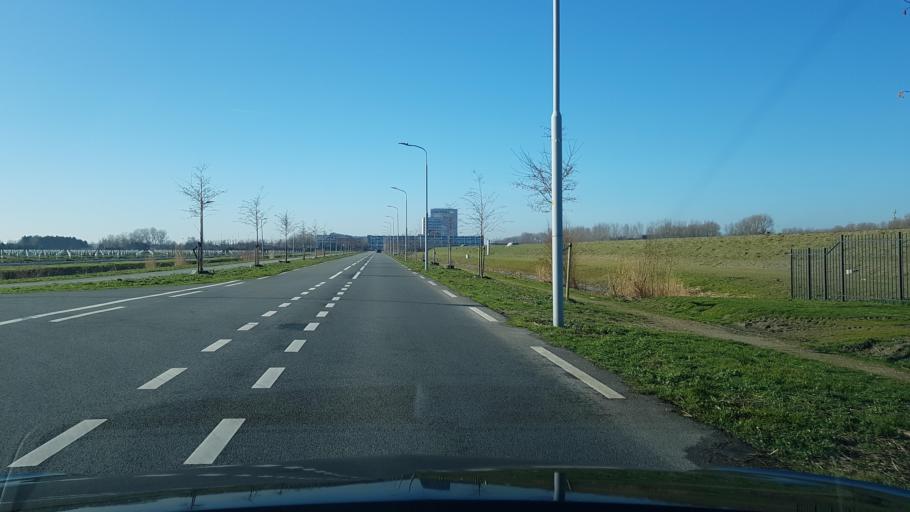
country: NL
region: North Holland
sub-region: Gemeente Haarlemmermeer
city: Hoofddorp
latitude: 52.2629
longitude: 4.6958
